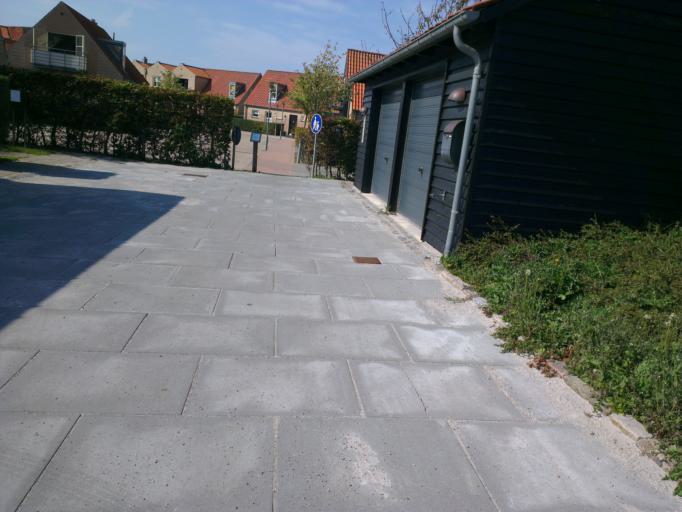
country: DK
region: Capital Region
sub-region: Frederikssund Kommune
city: Frederikssund
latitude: 55.8384
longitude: 12.0552
